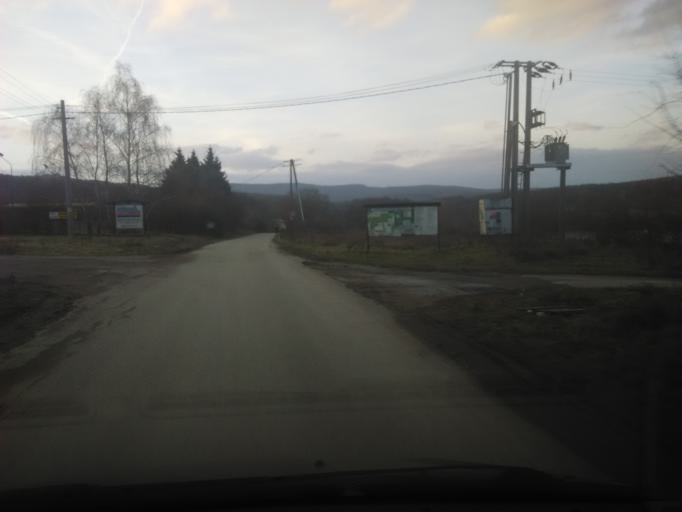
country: SK
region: Nitriansky
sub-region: Okres Nitra
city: Nitra
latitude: 48.3922
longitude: 18.2102
